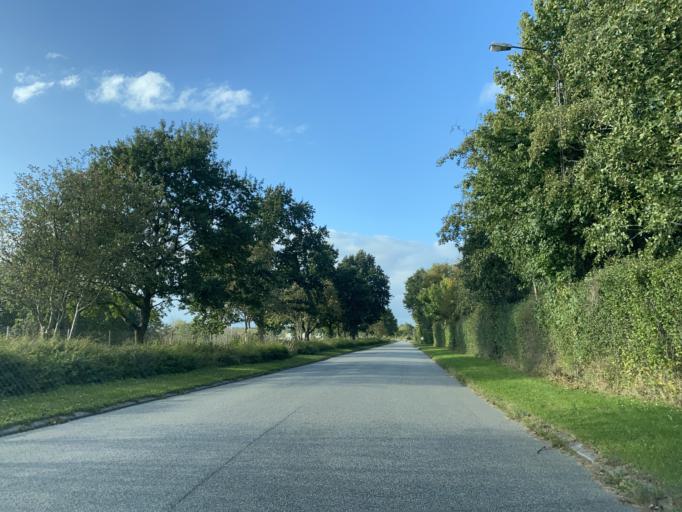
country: DK
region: Central Jutland
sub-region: Skanderborg Kommune
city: Ry
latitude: 56.1497
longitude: 9.8146
